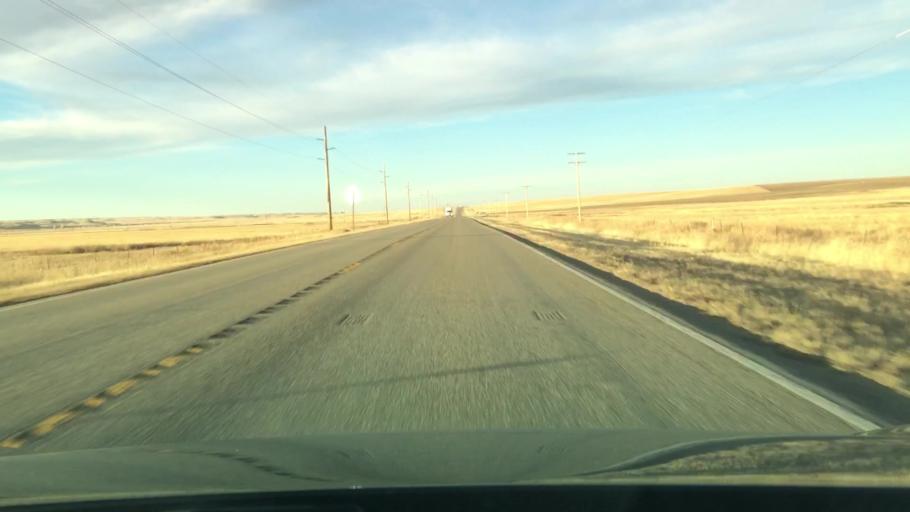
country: US
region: Montana
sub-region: Wheatland County
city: Harlowton
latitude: 46.8189
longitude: -109.7603
